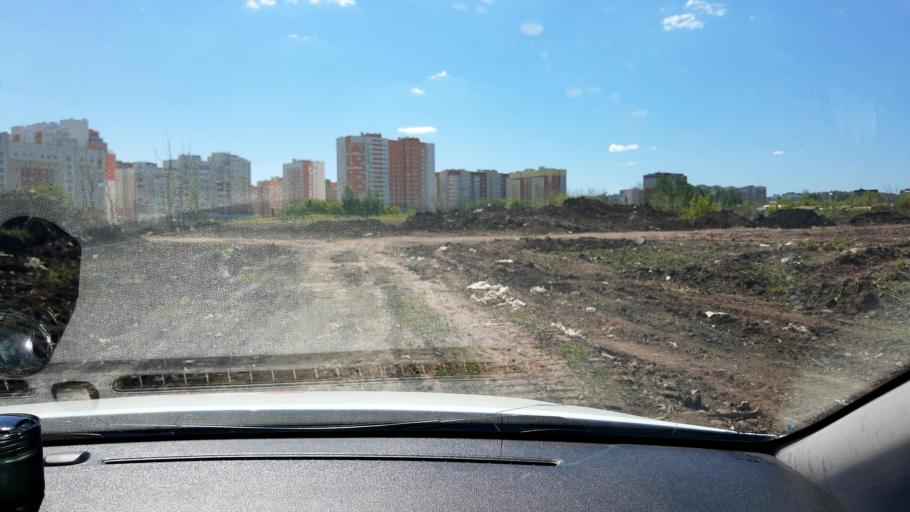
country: RU
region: Bashkortostan
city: Mikhaylovka
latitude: 54.7174
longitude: 55.8372
